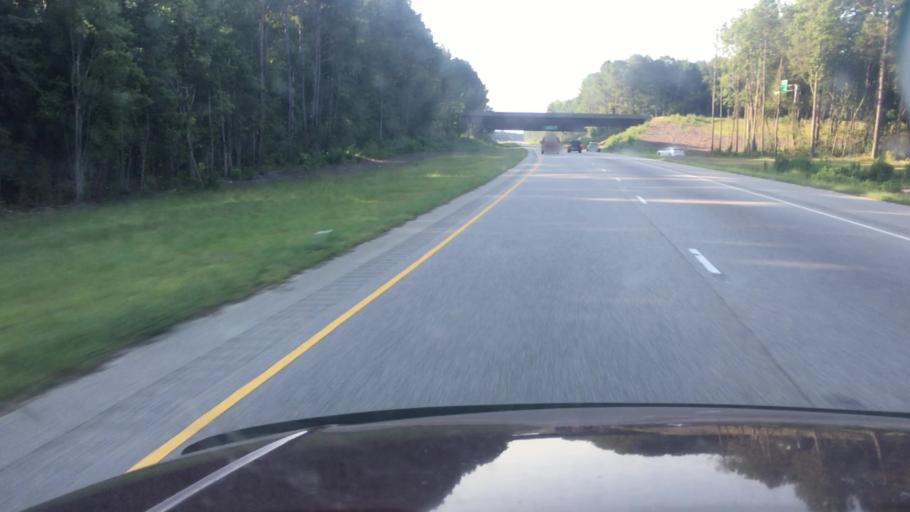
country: US
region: North Carolina
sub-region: Cumberland County
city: Fayetteville
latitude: 34.9787
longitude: -78.8586
